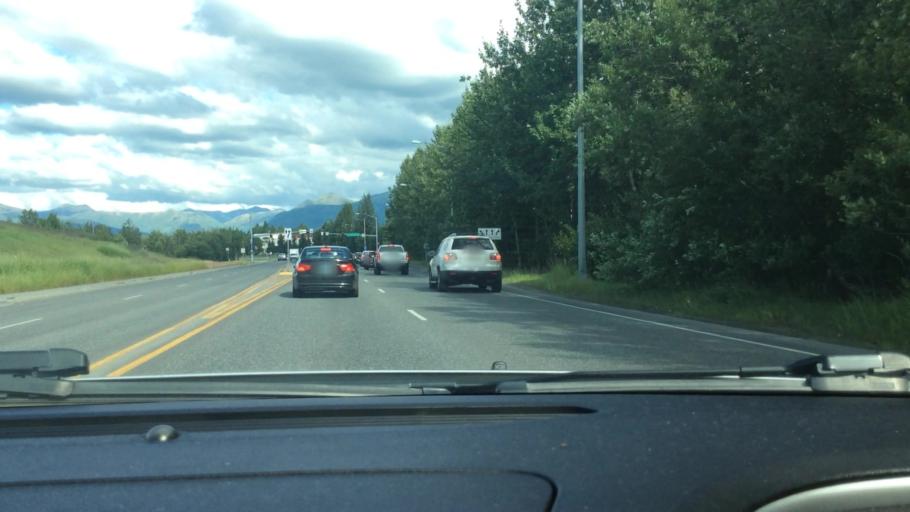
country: US
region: Alaska
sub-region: Anchorage Municipality
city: Anchorage
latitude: 61.2077
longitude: -149.8426
